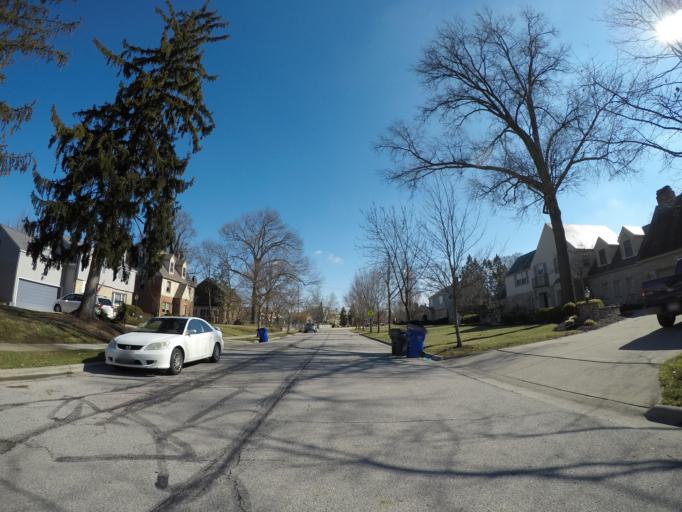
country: US
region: Ohio
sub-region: Franklin County
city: Upper Arlington
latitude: 39.9993
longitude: -83.0579
